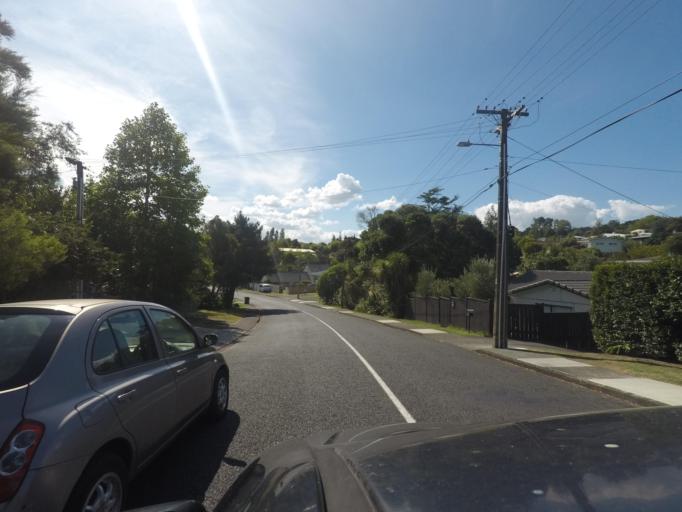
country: NZ
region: Auckland
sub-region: Auckland
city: Waitakere
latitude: -36.9247
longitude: 174.6599
